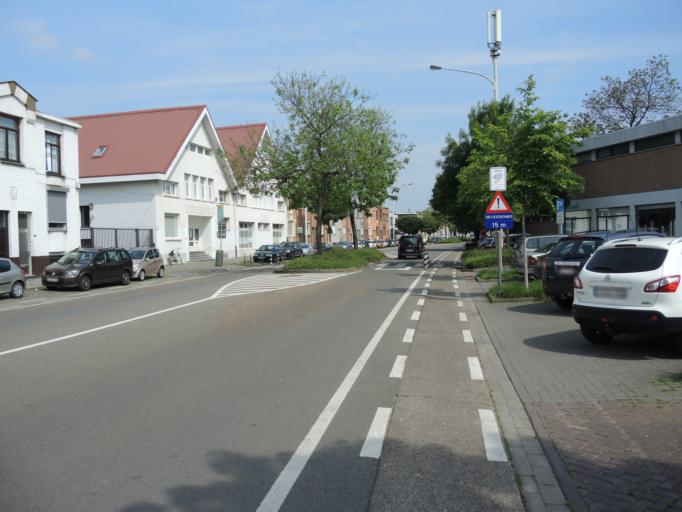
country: BE
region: Flanders
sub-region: Provincie Antwerpen
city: Borsbeek
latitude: 51.2281
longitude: 4.4547
